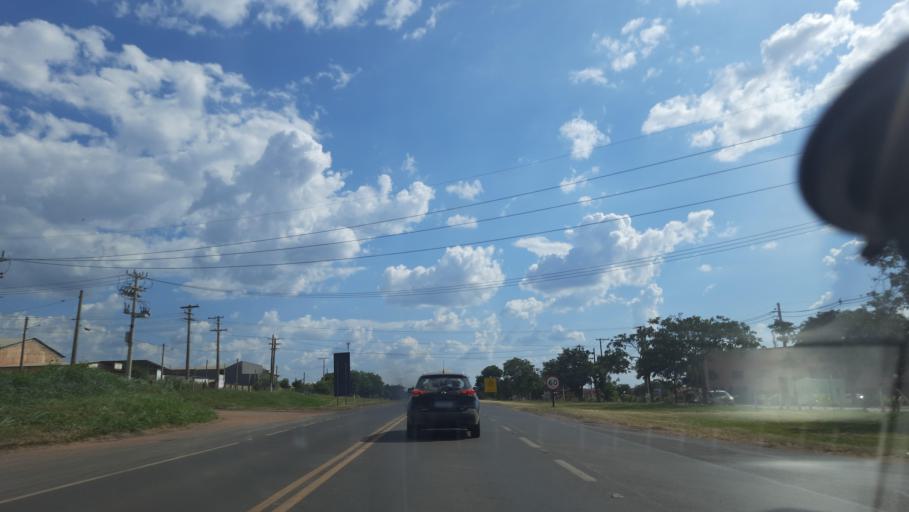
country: BR
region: Sao Paulo
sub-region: Vargem Grande Do Sul
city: Vargem Grande do Sul
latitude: -21.7321
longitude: -46.9684
